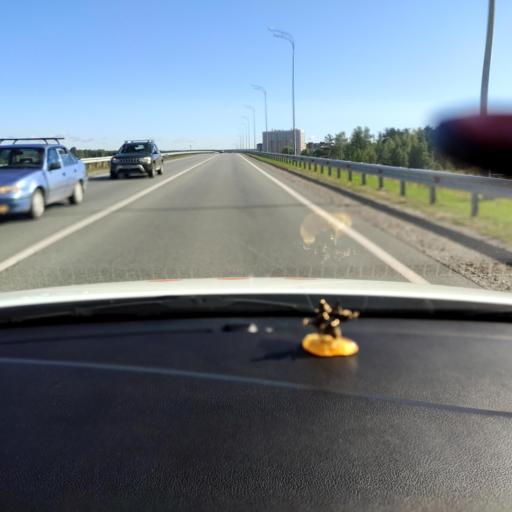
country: RU
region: Tatarstan
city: Stolbishchi
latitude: 55.6803
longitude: 49.1985
